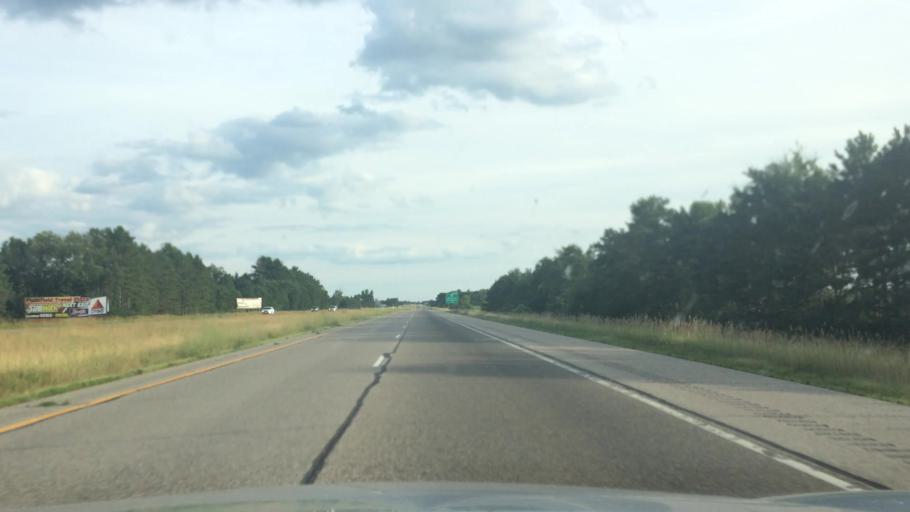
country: US
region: Wisconsin
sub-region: Portage County
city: Plover
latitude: 44.2369
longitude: -89.5245
